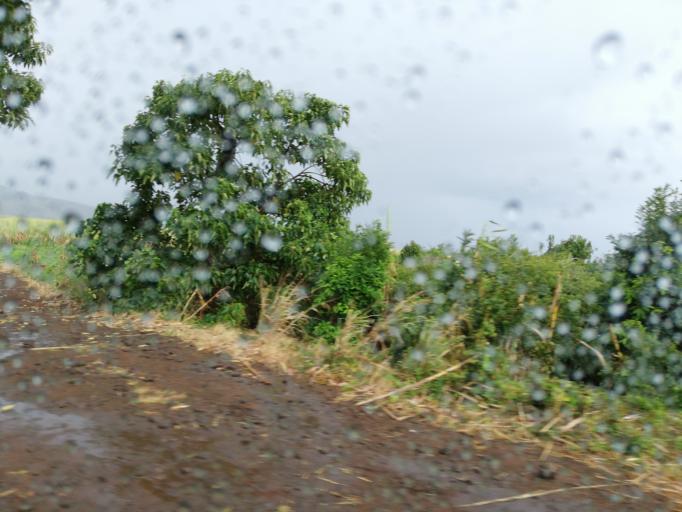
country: MU
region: Pamplemousses
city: Long Mountain
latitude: -20.1299
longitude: 57.5658
